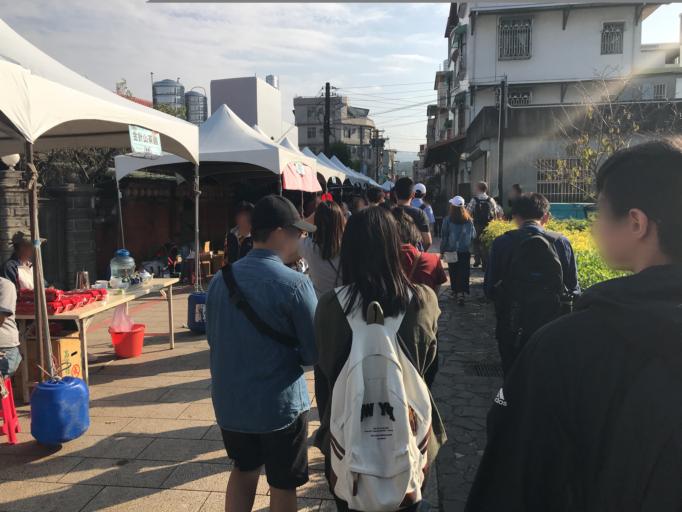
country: TW
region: Taiwan
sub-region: Hsinchu
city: Hsinchu
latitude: 24.7006
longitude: 121.0577
